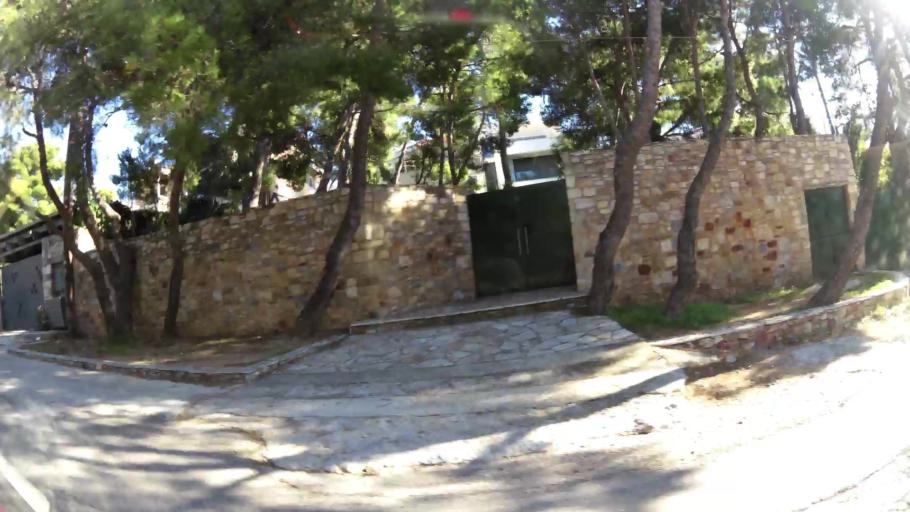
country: GR
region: Attica
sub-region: Nomarchia Athinas
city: Penteli
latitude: 38.0421
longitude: 23.8822
